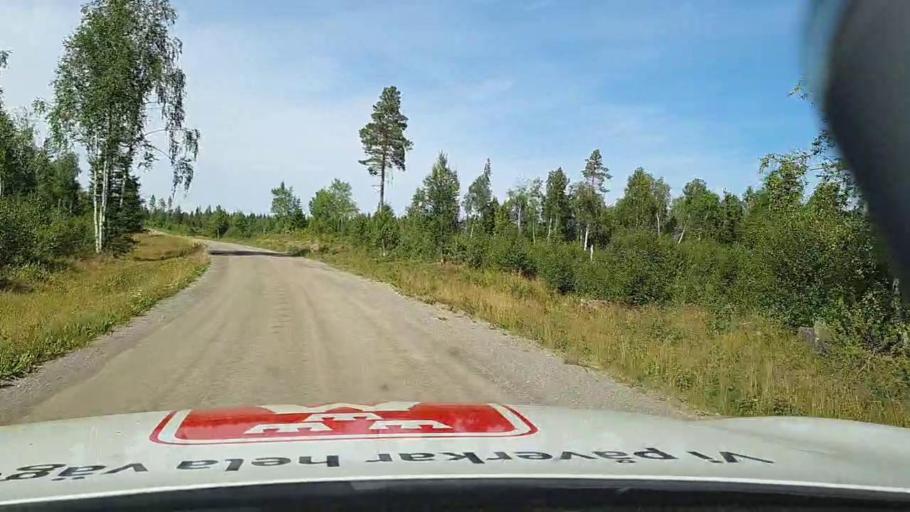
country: SE
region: Jaemtland
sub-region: Stroemsunds Kommun
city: Stroemsund
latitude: 63.7165
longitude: 15.2982
